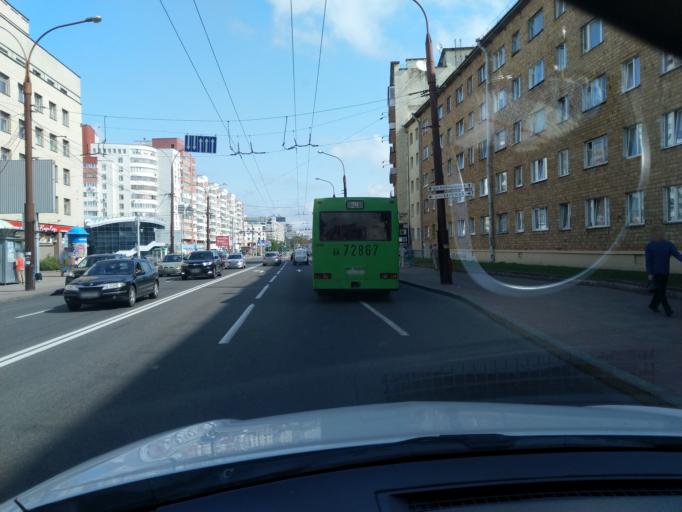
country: BY
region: Minsk
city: Minsk
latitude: 53.9187
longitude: 27.5746
